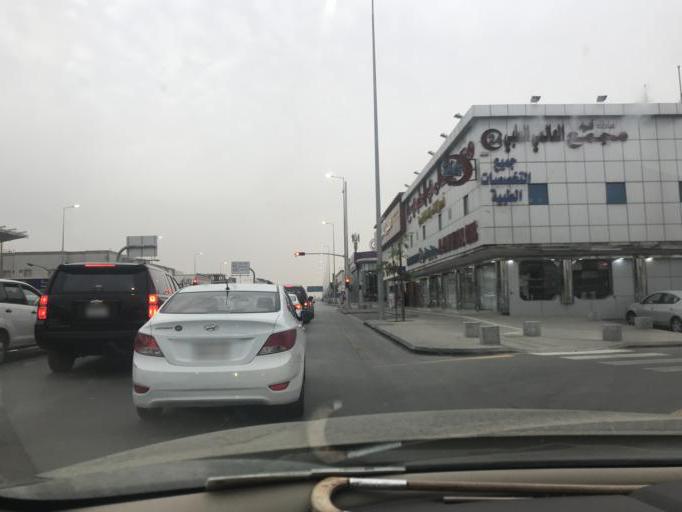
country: SA
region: Ar Riyad
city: Riyadh
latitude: 24.7619
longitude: 46.7637
